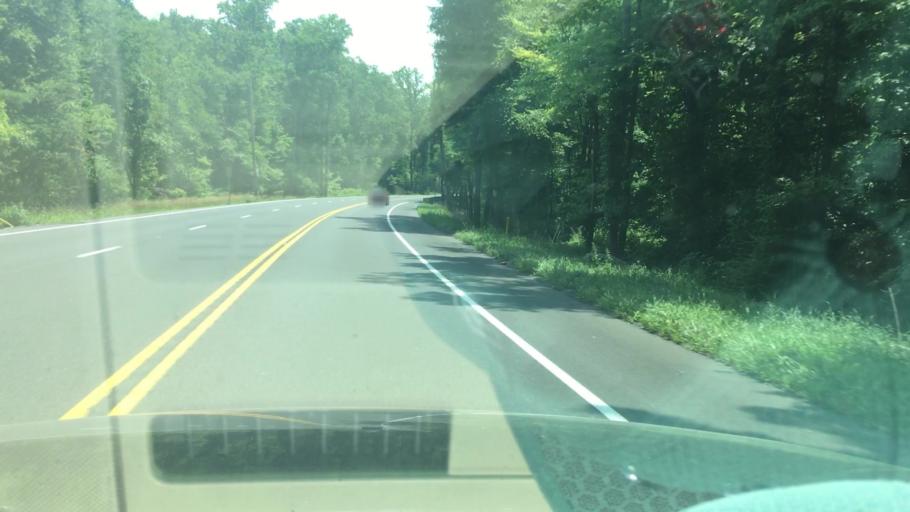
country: US
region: Pennsylvania
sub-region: Carbon County
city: Lehighton
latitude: 40.7169
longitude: -75.7706
